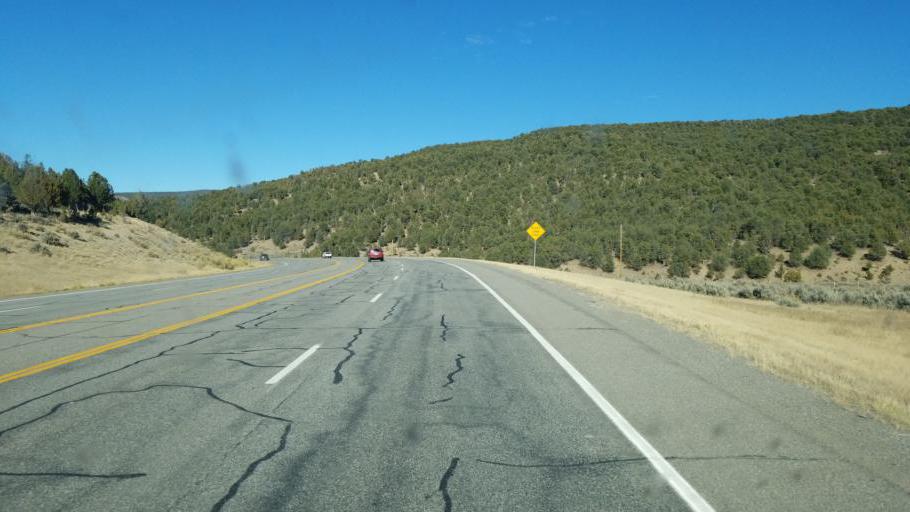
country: US
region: Colorado
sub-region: Ouray County
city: Ouray
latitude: 38.2102
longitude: -107.7280
